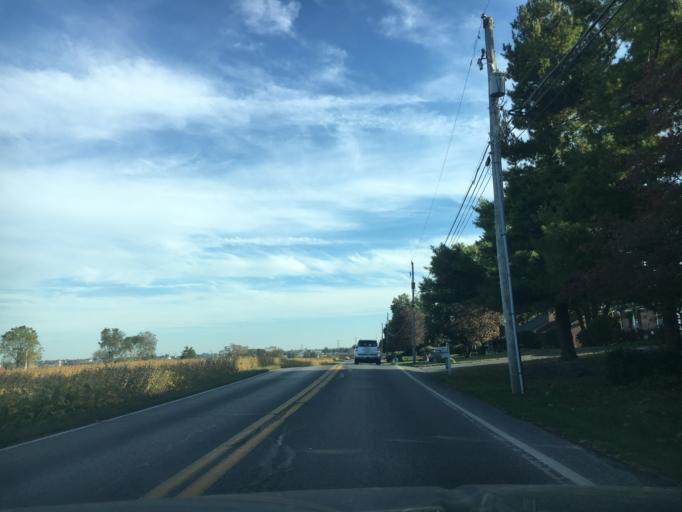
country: US
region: Pennsylvania
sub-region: Lancaster County
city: Brownstown
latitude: 40.1244
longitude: -76.1838
